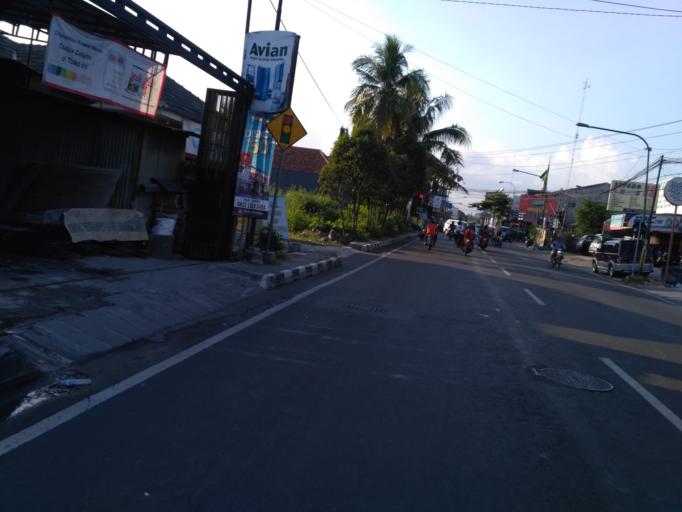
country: ID
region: Daerah Istimewa Yogyakarta
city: Yogyakarta
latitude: -7.8266
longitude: 110.3901
